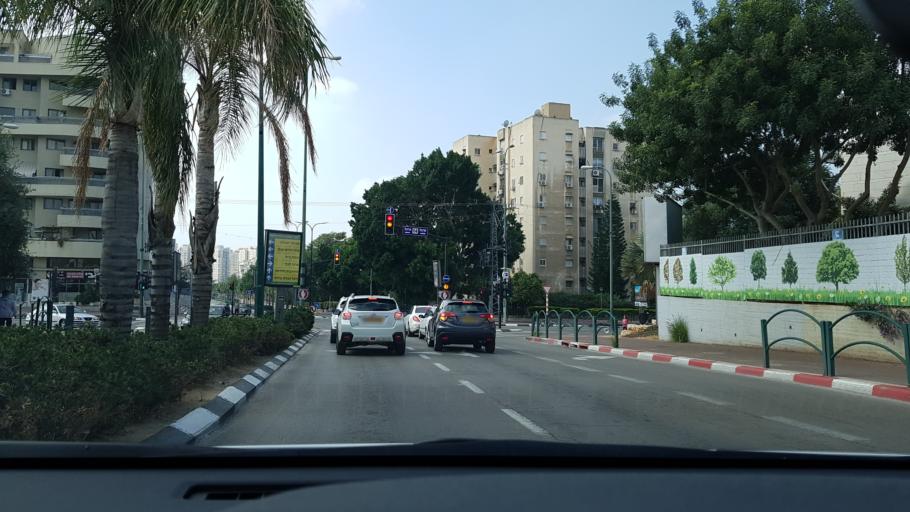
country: IL
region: Central District
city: Mazkeret Batya
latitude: 31.8835
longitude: 34.8173
